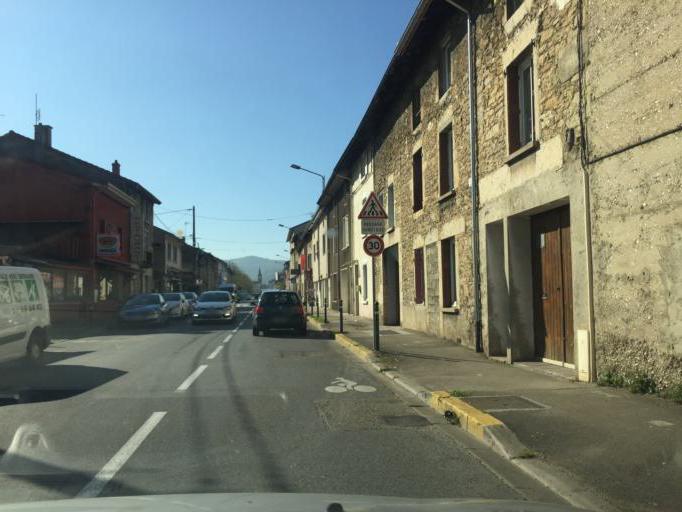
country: FR
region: Rhone-Alpes
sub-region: Departement de l'Ain
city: Amberieu-en-Bugey
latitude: 45.9658
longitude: 5.3551
